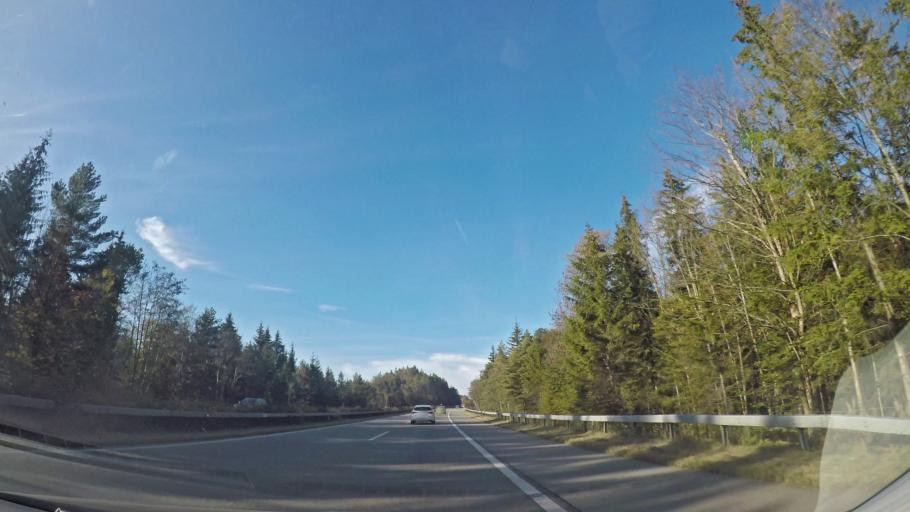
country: CH
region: Bern
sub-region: Thun District
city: Thun
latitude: 46.7194
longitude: 7.6107
